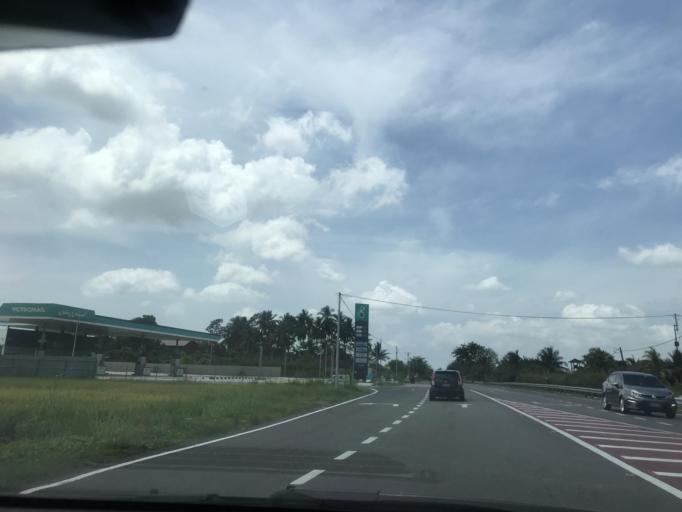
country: MY
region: Kelantan
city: Kota Bharu
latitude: 6.1524
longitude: 102.2071
